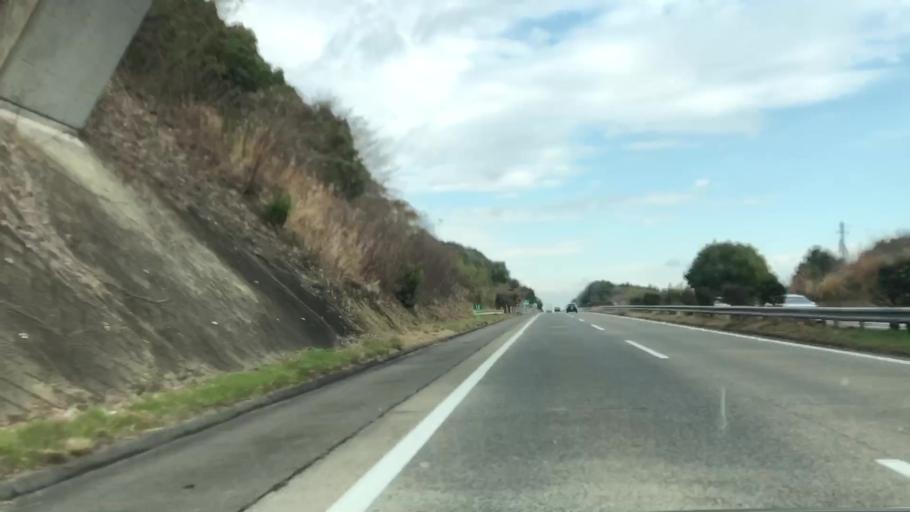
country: JP
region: Saga Prefecture
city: Kanzakimachi-kanzaki
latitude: 33.3574
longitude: 130.4247
